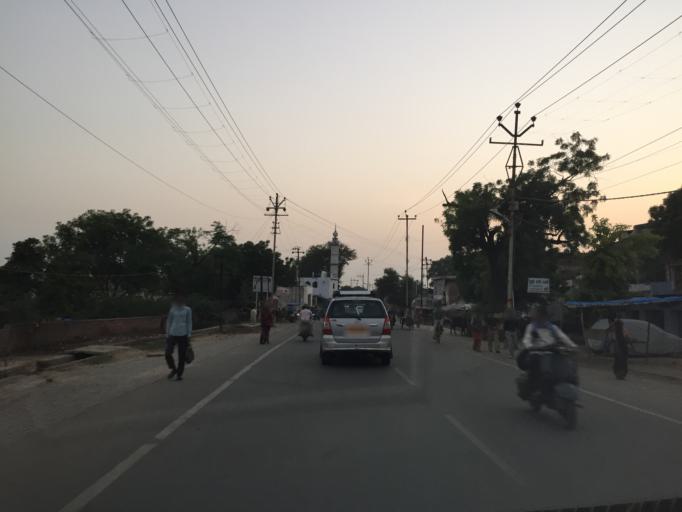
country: IN
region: Uttar Pradesh
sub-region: Agra
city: Dayal Bagh
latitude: 27.2075
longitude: 78.0626
